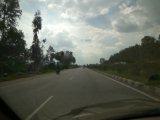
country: IN
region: Karnataka
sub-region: Kolar
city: Kolar
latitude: 13.1222
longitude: 78.0684
